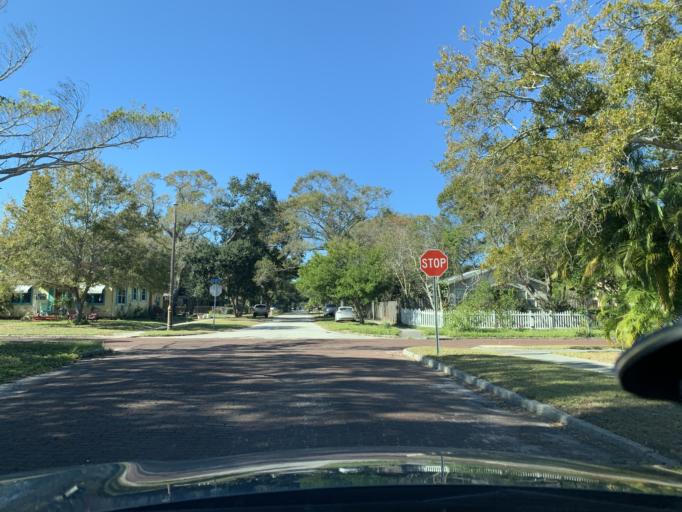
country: US
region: Florida
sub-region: Pinellas County
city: Gulfport
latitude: 27.7502
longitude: -82.7050
